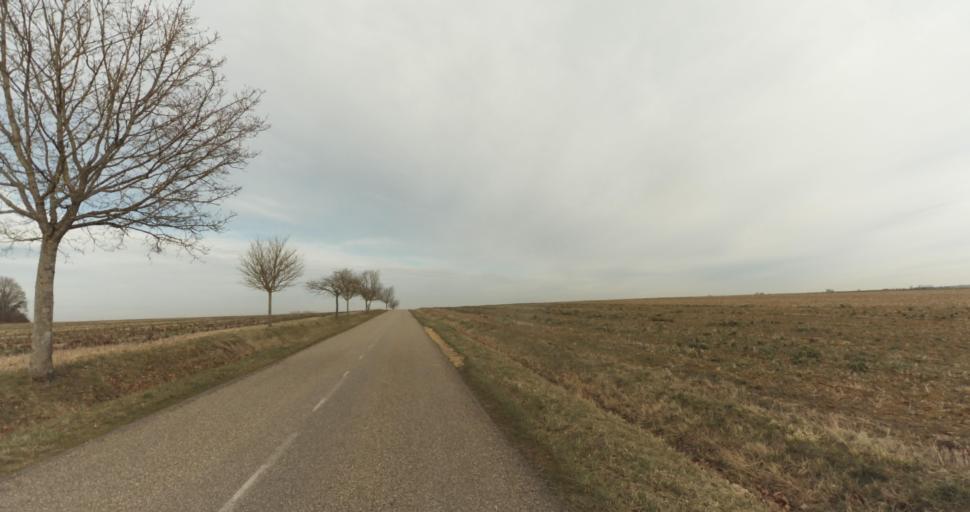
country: FR
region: Lorraine
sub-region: Departement de Meurthe-et-Moselle
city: Conflans-en-Jarnisy
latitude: 49.1355
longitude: 5.8527
